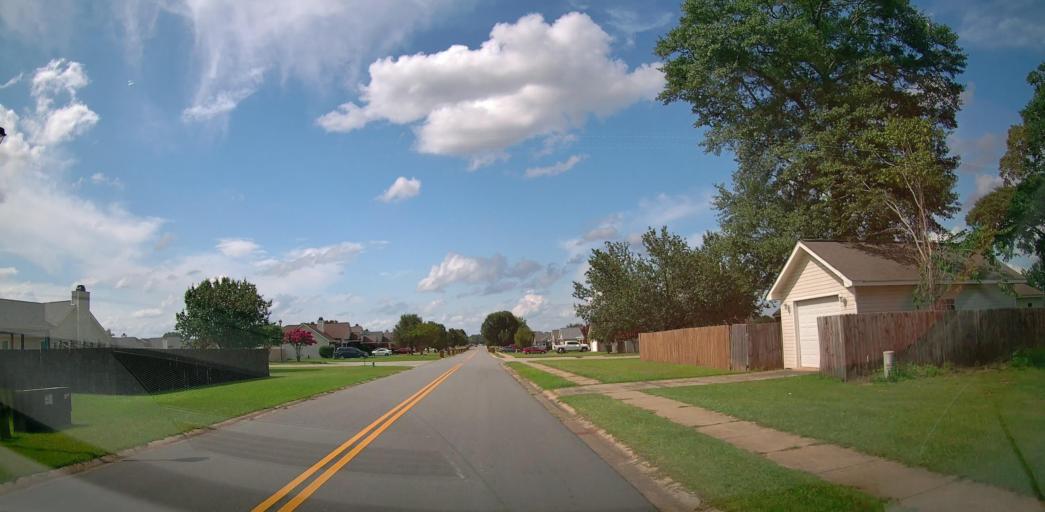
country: US
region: Georgia
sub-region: Houston County
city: Centerville
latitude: 32.5741
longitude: -83.7004
